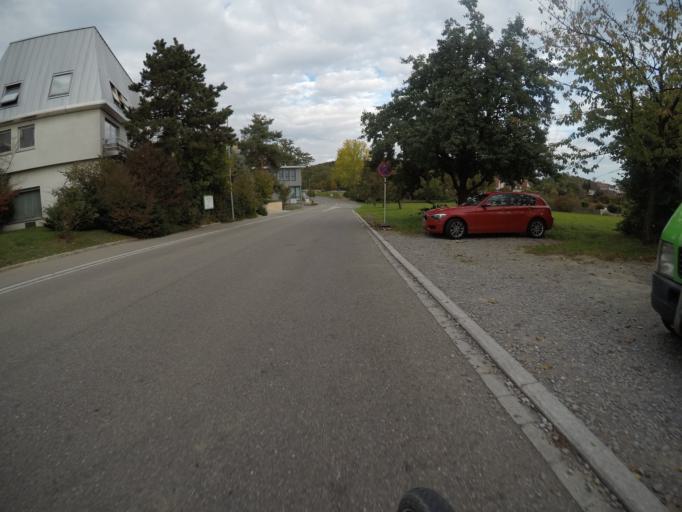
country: DE
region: Baden-Wuerttemberg
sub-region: Regierungsbezirk Stuttgart
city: Ehningen
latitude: 48.6638
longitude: 8.9550
